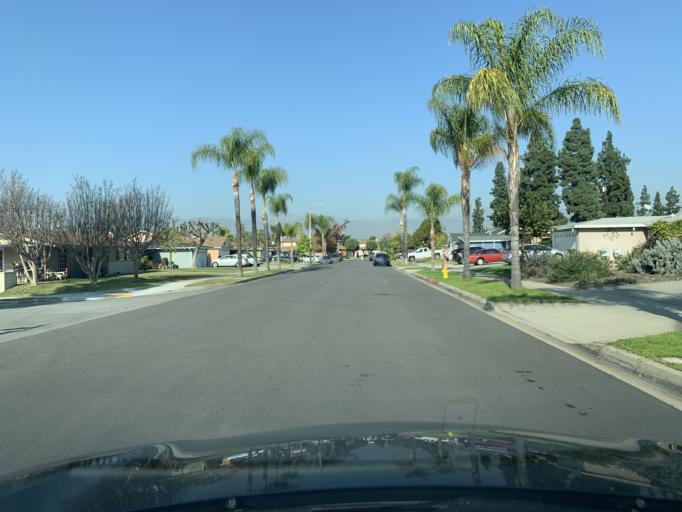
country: US
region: California
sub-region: Los Angeles County
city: Covina
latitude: 34.0759
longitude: -117.8839
